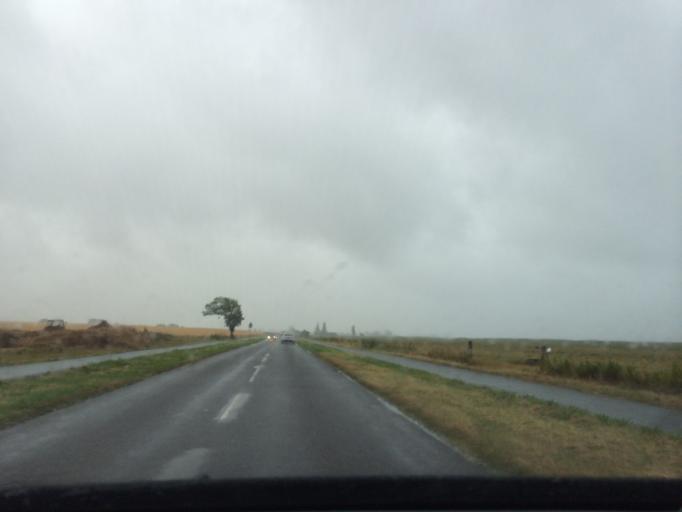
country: DK
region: Zealand
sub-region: Vordingborg Kommune
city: Stege
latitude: 55.0190
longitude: 12.2901
